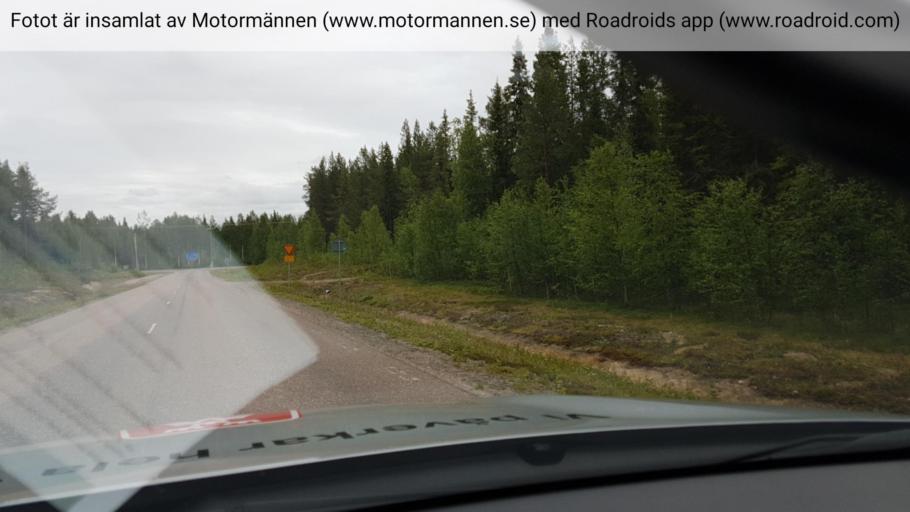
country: SE
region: Norrbotten
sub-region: Overkalix Kommun
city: OEverkalix
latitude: 67.0721
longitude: 22.5178
